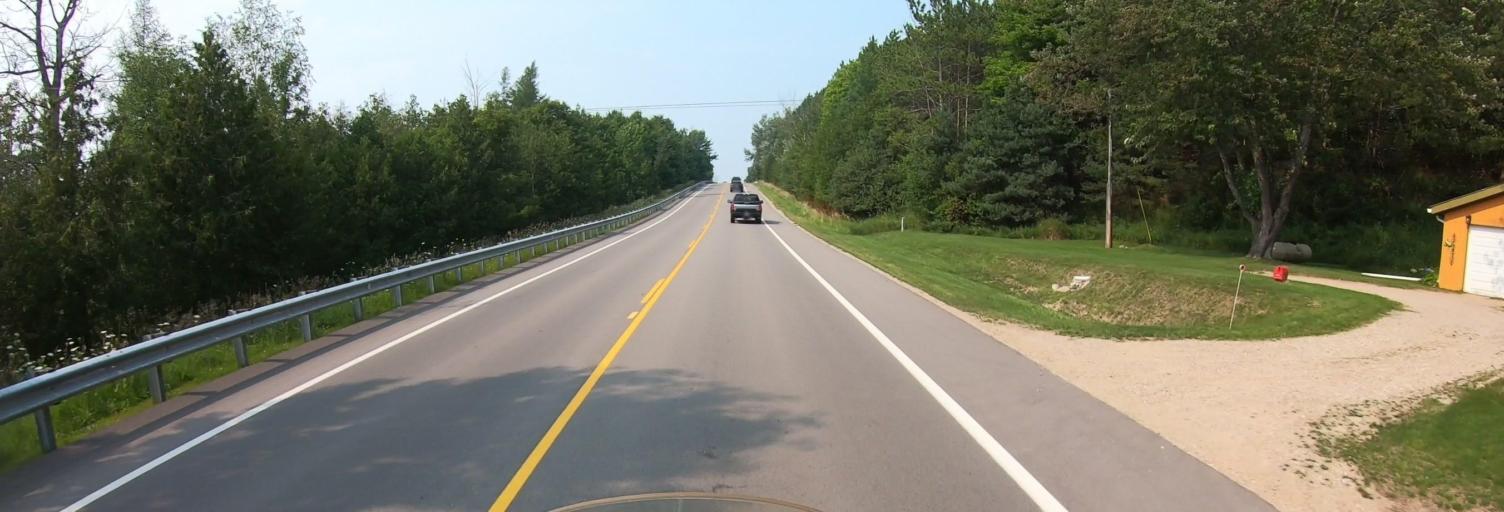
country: US
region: Michigan
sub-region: Charlevoix County
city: Charlevoix
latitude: 45.2393
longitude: -85.2613
